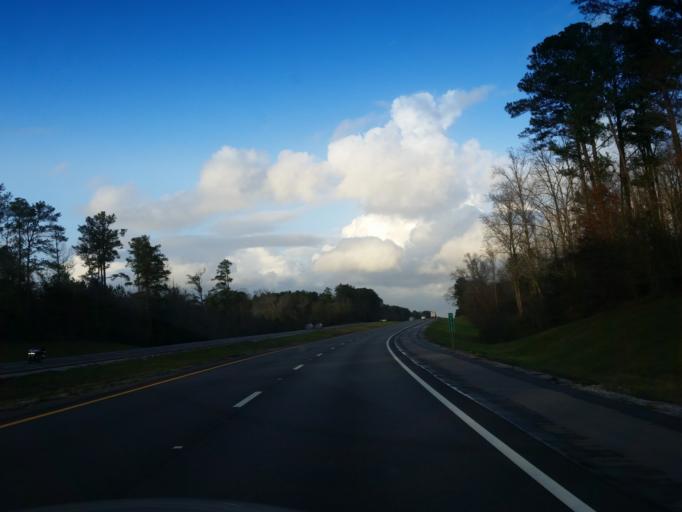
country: US
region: Mississippi
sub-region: Jones County
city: Sharon
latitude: 31.8747
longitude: -89.0446
